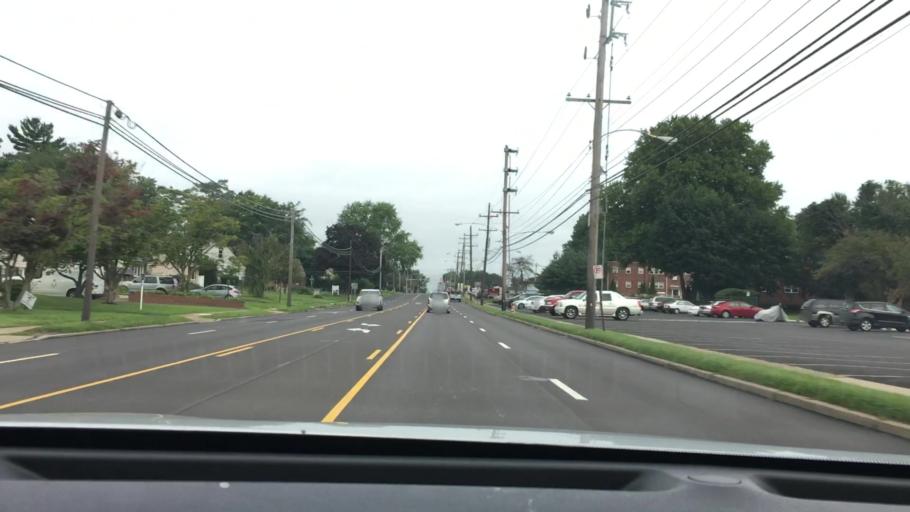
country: US
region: Pennsylvania
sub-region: Bucks County
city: Warminster Heights
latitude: 40.1779
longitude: -75.0825
